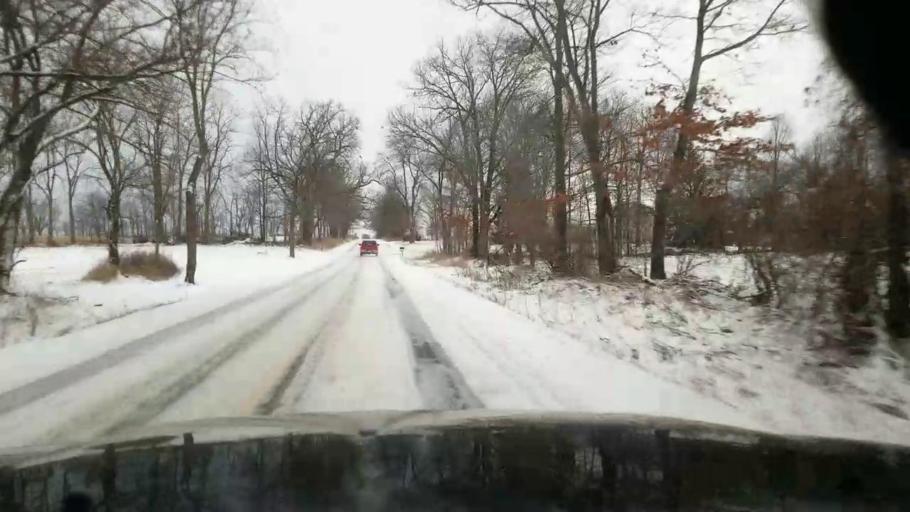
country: US
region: Michigan
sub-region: Jackson County
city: Spring Arbor
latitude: 42.1535
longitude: -84.4993
